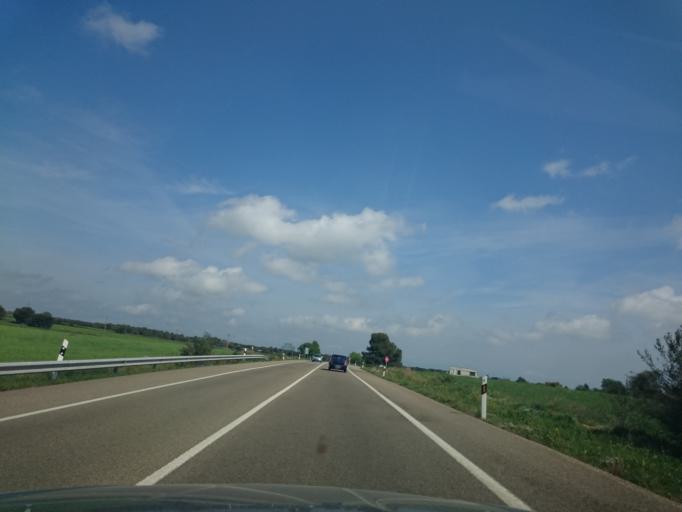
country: ES
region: Catalonia
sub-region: Provincia de Girona
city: Pontos
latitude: 42.1892
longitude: 2.9304
